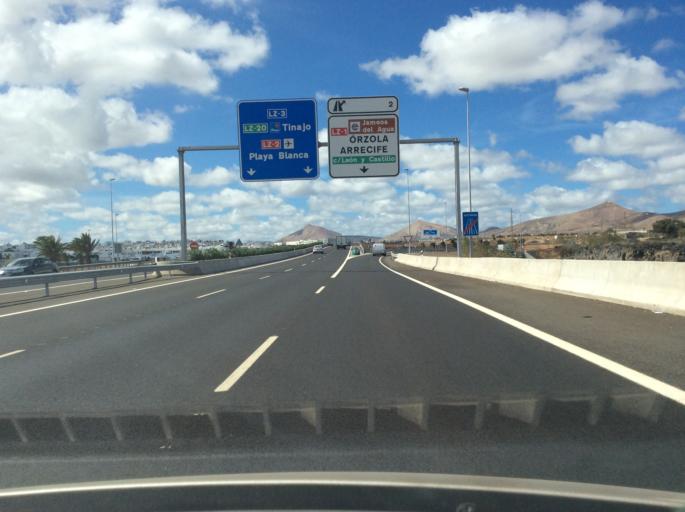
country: ES
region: Canary Islands
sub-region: Provincia de Las Palmas
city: Arrecife
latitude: 28.9813
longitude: -13.5420
